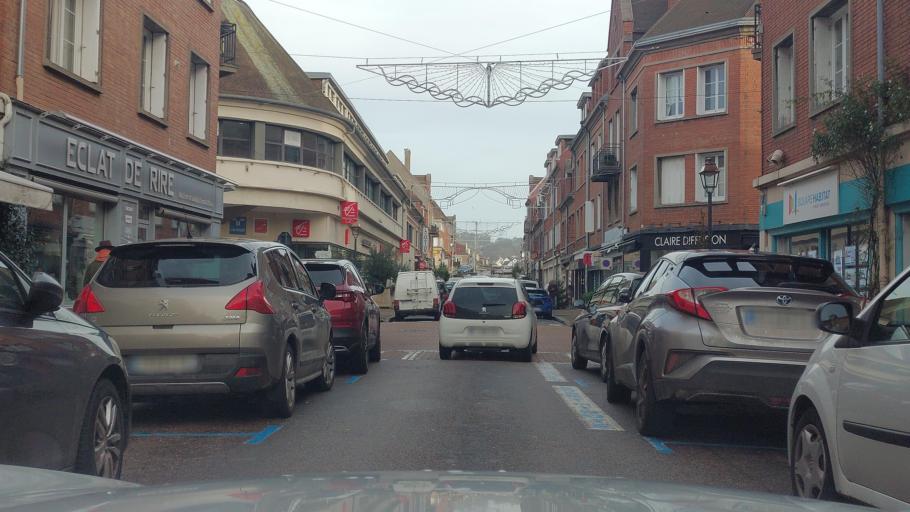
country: FR
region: Haute-Normandie
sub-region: Departement de la Seine-Maritime
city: Eu
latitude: 50.0508
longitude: 1.4207
